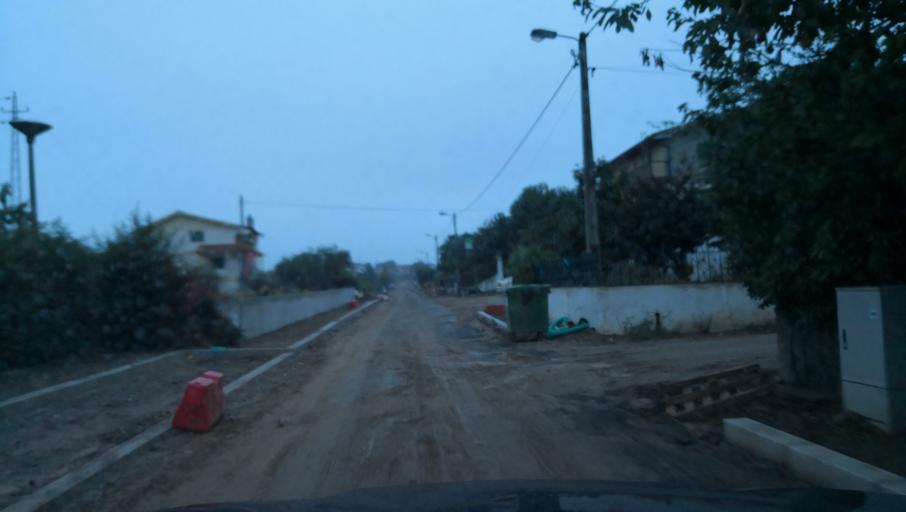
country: PT
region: Vila Real
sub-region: Sabrosa
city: Sabrosa
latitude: 41.2648
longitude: -7.6133
